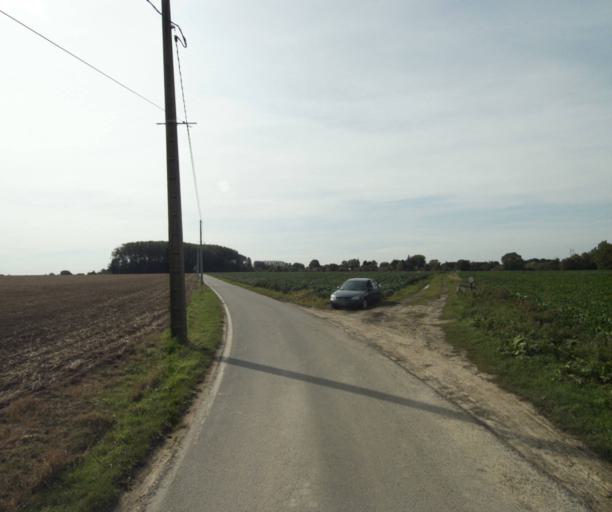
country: FR
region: Nord-Pas-de-Calais
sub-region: Departement du Nord
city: Ennetieres-en-Weppes
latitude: 50.6252
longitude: 2.9371
